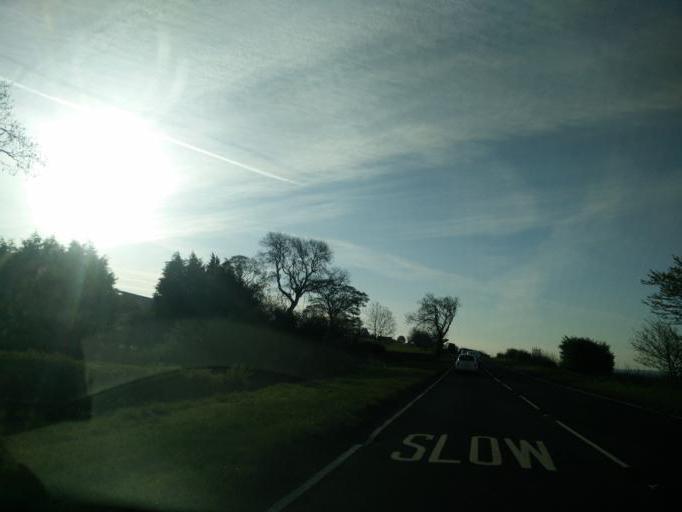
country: GB
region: England
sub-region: County Durham
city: Crook
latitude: 54.6786
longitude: -1.7287
